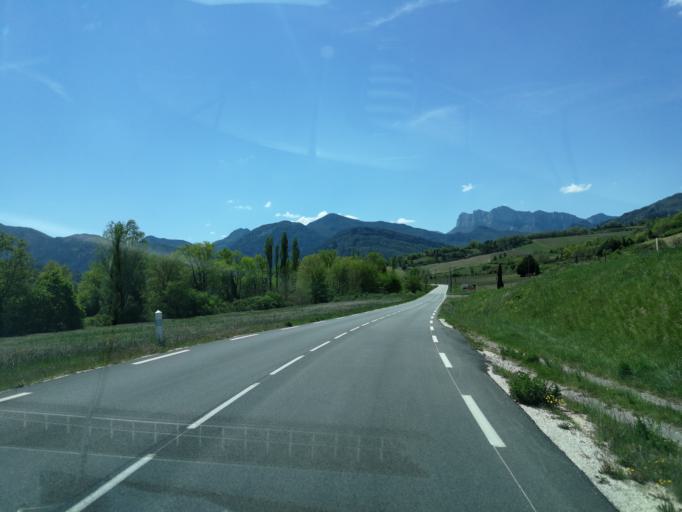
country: FR
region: Rhone-Alpes
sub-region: Departement de la Drome
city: Die
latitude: 44.7239
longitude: 5.2676
